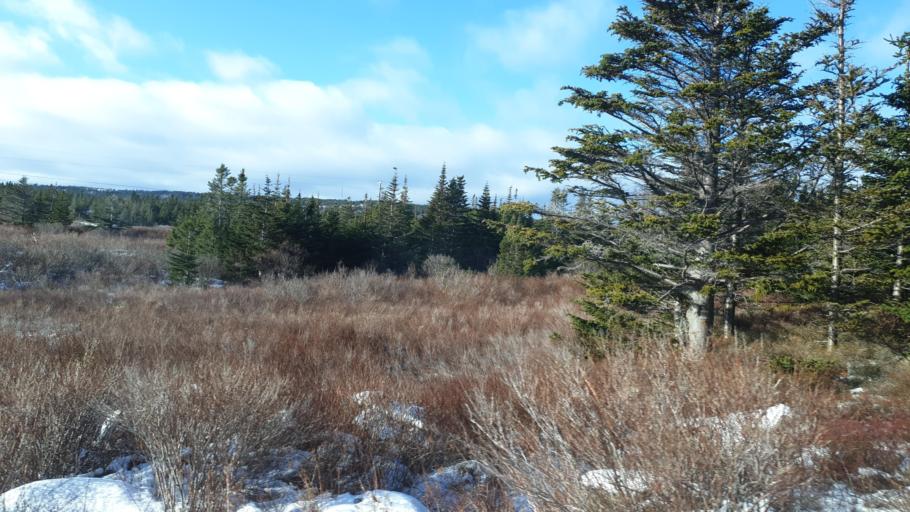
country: CA
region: Newfoundland and Labrador
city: Bonavista
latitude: 48.6268
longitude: -53.0341
